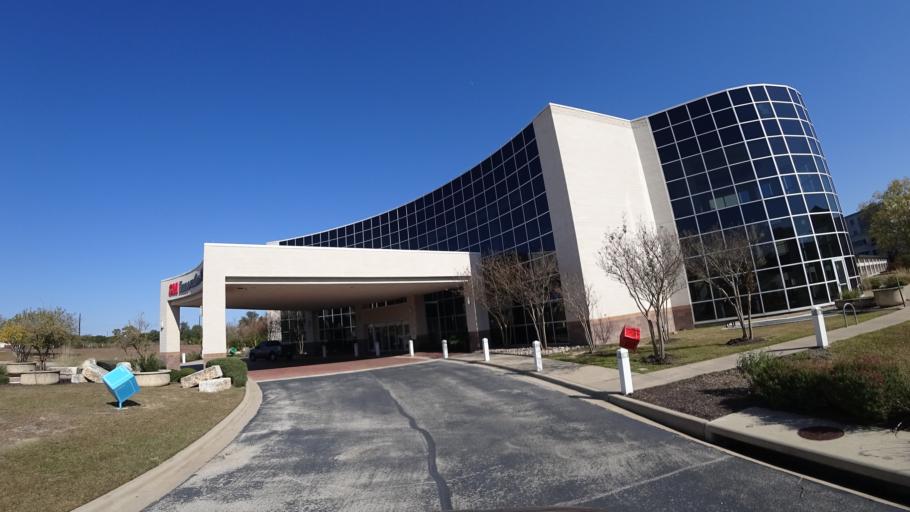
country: US
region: Texas
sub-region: Williamson County
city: Anderson Mill
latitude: 30.3953
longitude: -97.8420
